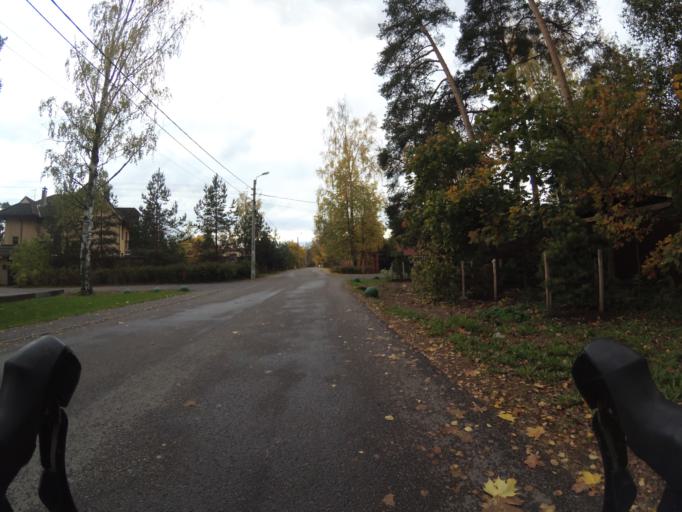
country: RU
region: St.-Petersburg
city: Lakhtinskiy
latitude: 59.9977
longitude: 30.1465
